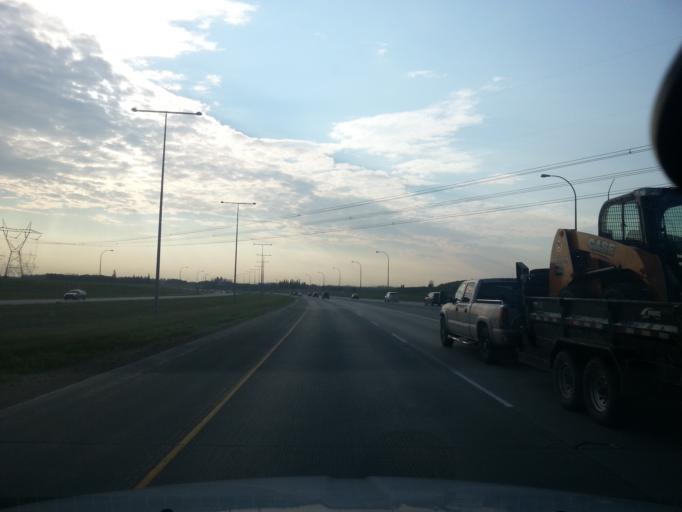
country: CA
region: Alberta
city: Edmonton
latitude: 53.4292
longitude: -113.5776
